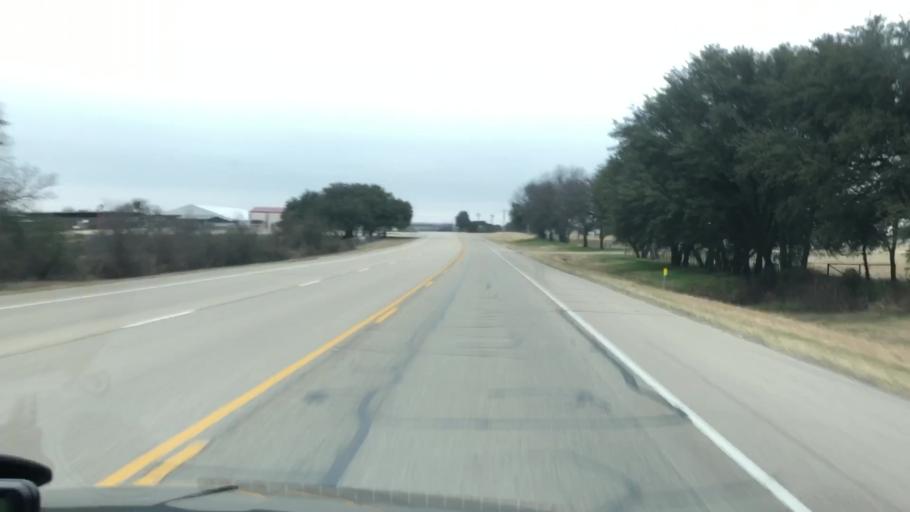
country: US
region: Texas
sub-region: Hamilton County
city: Hamilton
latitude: 31.7519
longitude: -98.1185
